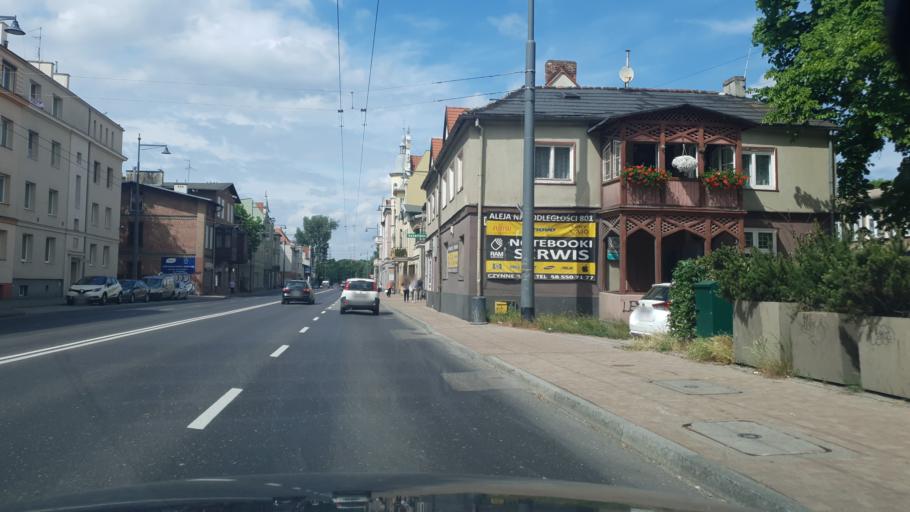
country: PL
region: Pomeranian Voivodeship
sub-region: Sopot
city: Sopot
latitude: 54.4437
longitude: 18.5596
